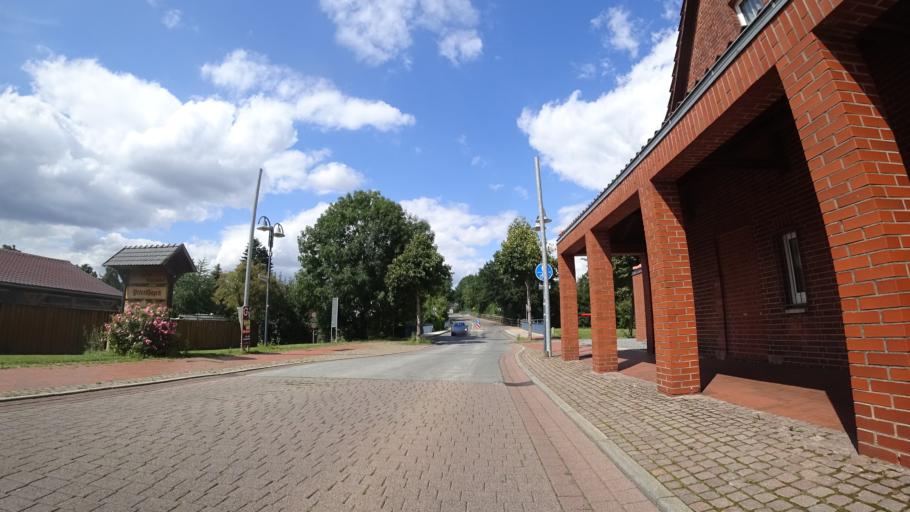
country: DE
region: North Rhine-Westphalia
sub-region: Regierungsbezirk Detmold
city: Petershagen
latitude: 52.3792
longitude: 8.9696
